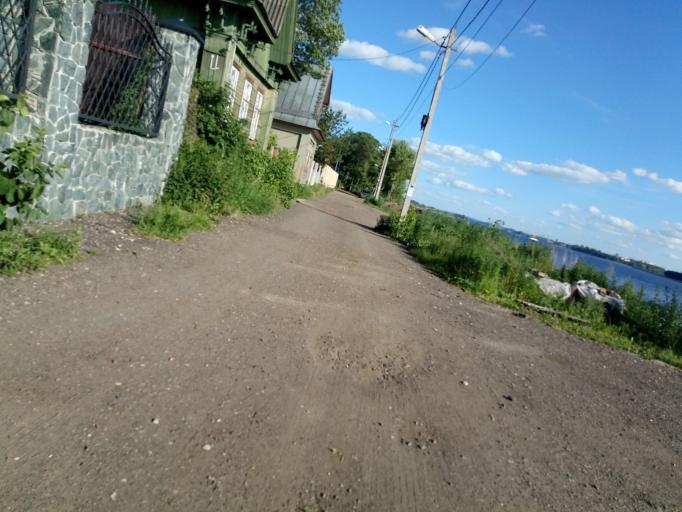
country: RU
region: Jaroslavl
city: Yaroslavl
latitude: 57.6347
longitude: 39.9048
